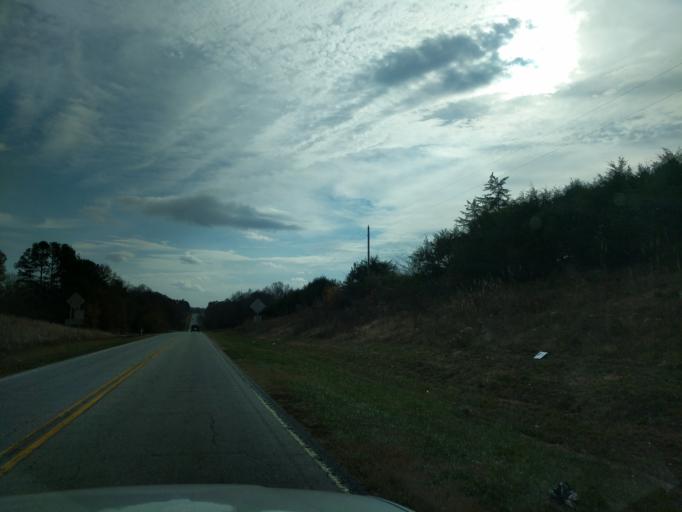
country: US
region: South Carolina
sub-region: Oconee County
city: Westminster
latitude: 34.6334
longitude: -83.0479
